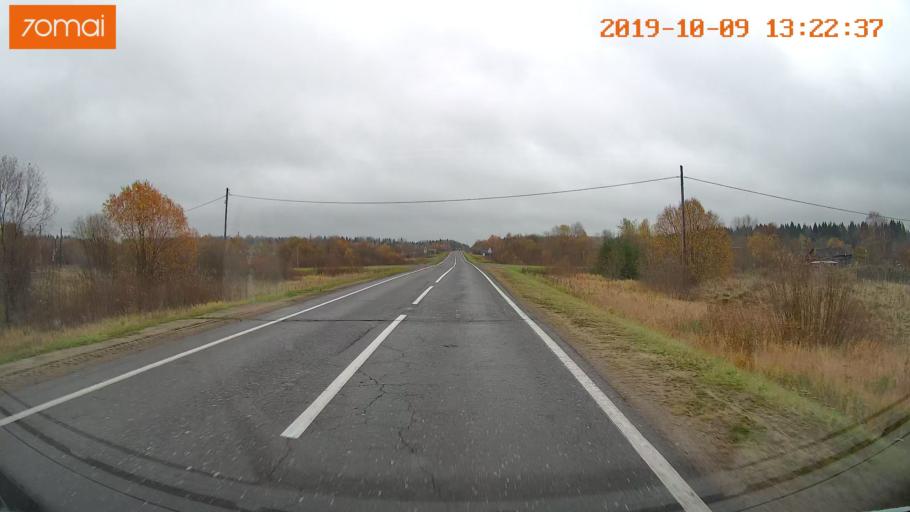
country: RU
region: Jaroslavl
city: Lyubim
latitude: 58.3392
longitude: 40.8692
